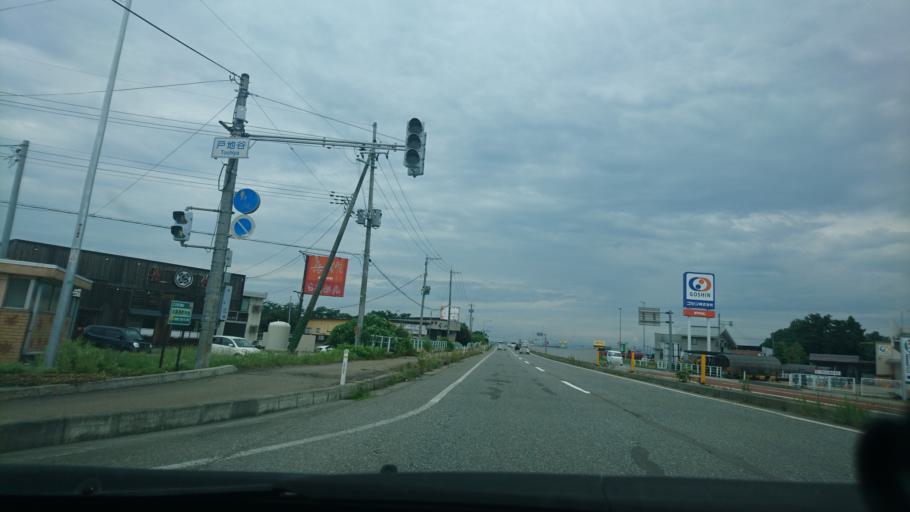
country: JP
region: Akita
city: Omagari
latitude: 39.4655
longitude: 140.4896
